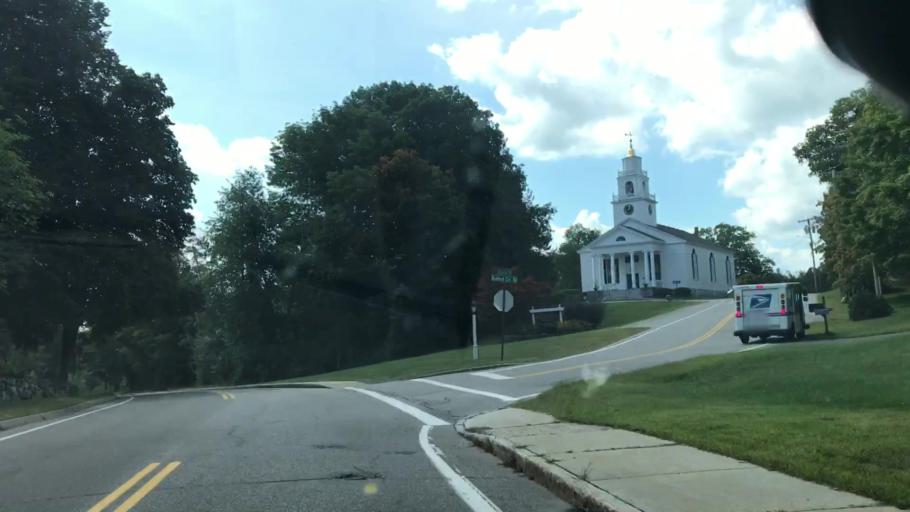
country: US
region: New Hampshire
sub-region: Hillsborough County
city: Bedford
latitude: 42.9472
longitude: -71.5156
